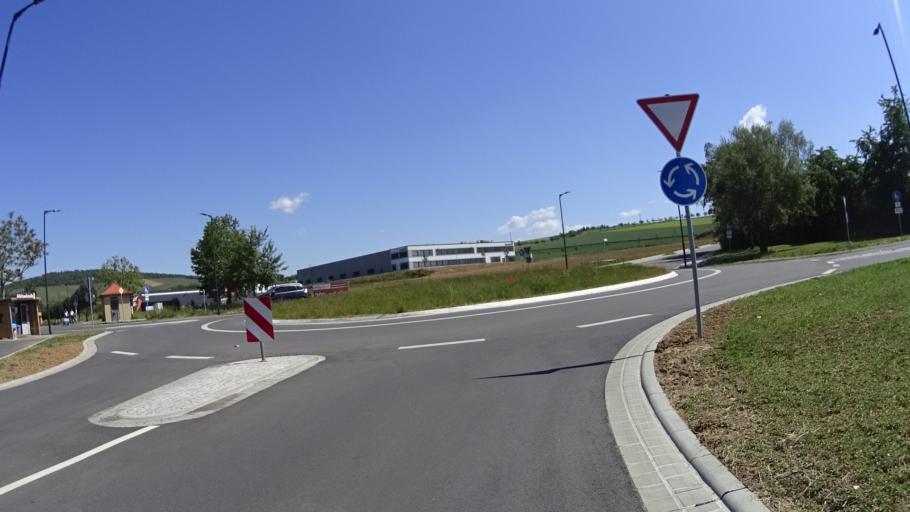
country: DE
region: Baden-Wuerttemberg
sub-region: Regierungsbezirk Stuttgart
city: Weikersheim
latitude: 49.4883
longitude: 9.9019
